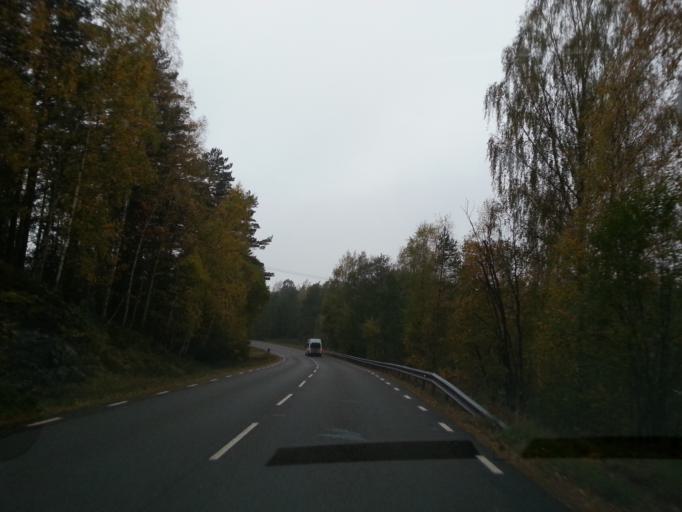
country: SE
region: OEstergoetland
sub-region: Norrkopings Kommun
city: Krokek
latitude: 58.6734
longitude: 16.3303
